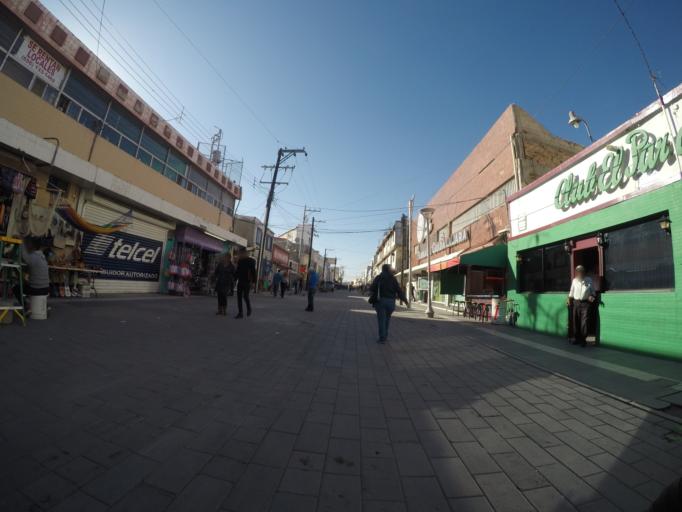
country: MX
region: Chihuahua
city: Ciudad Juarez
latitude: 31.7391
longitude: -106.4849
